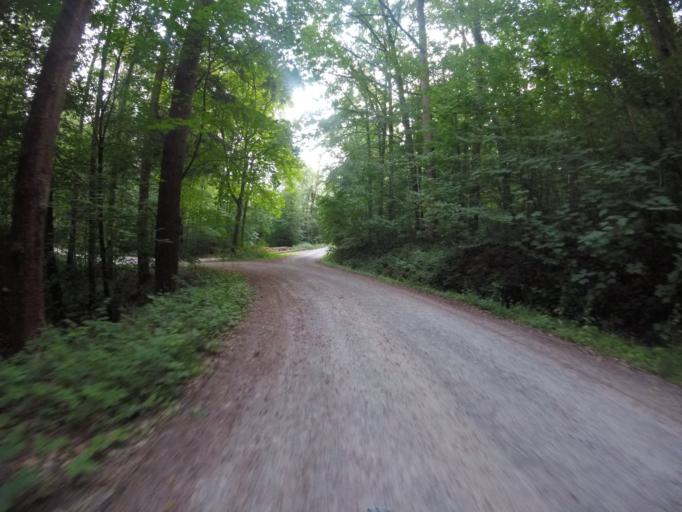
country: DE
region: Baden-Wuerttemberg
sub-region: Regierungsbezirk Stuttgart
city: Oppenweiler
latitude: 48.9719
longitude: 9.4894
